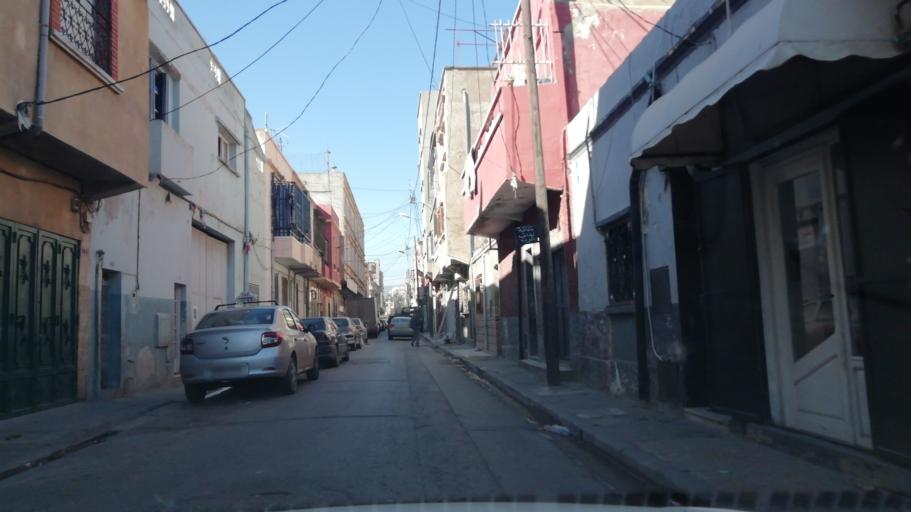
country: DZ
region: Oran
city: Oran
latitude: 35.6961
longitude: -0.6241
